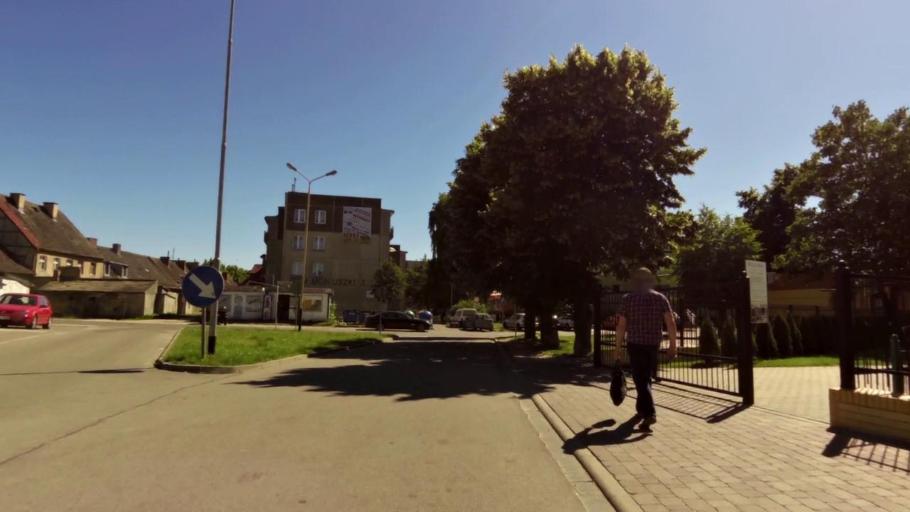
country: PL
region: West Pomeranian Voivodeship
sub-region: Powiat bialogardzki
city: Karlino
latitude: 54.0379
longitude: 15.8794
